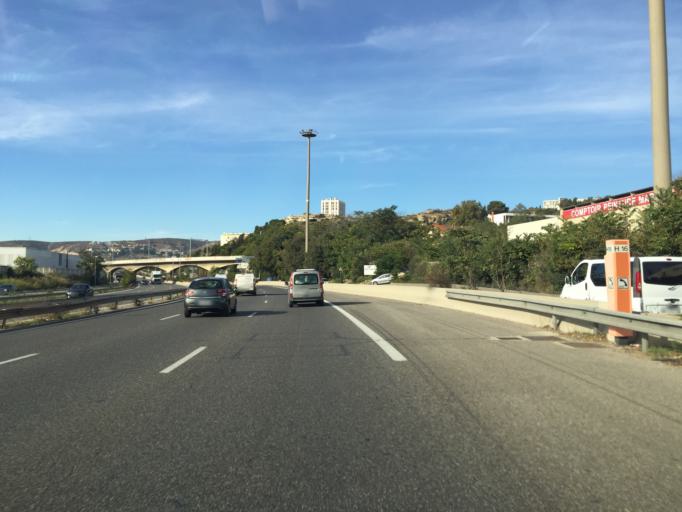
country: FR
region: Provence-Alpes-Cote d'Azur
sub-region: Departement des Bouches-du-Rhone
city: Marseille 16
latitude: 43.3412
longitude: 5.3485
